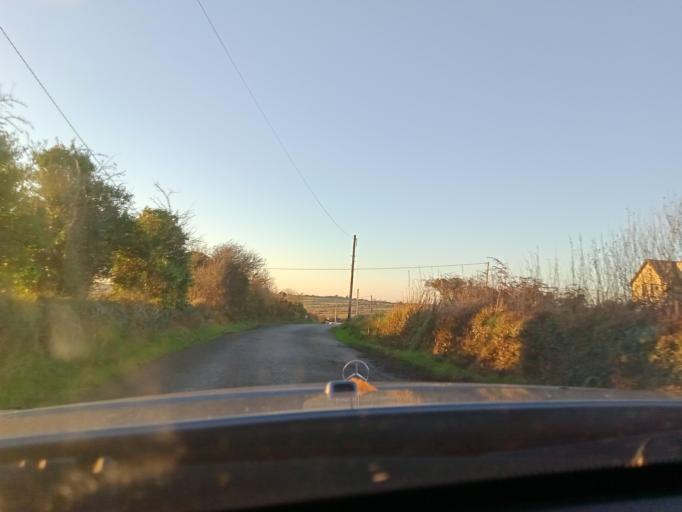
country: IE
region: Munster
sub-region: Waterford
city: Waterford
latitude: 52.3665
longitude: -7.1164
